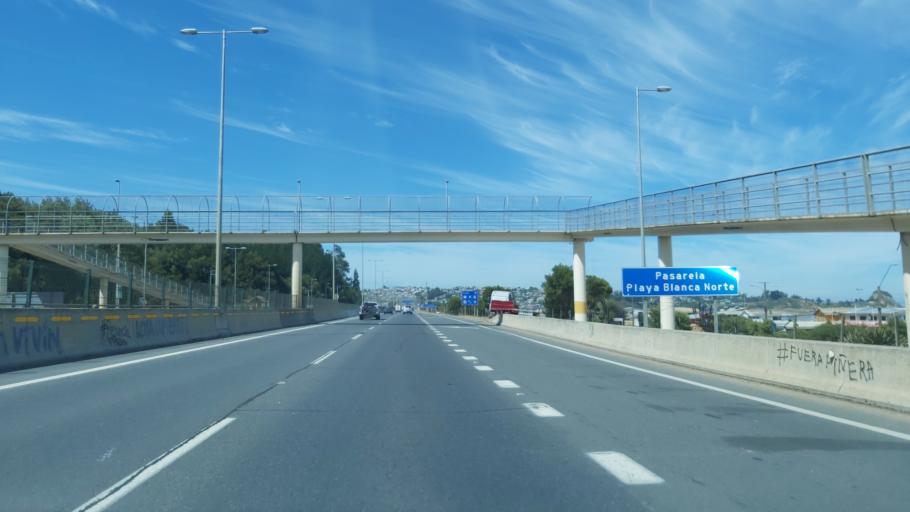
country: CL
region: Biobio
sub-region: Provincia de Concepcion
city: Coronel
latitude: -37.0630
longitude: -73.1415
